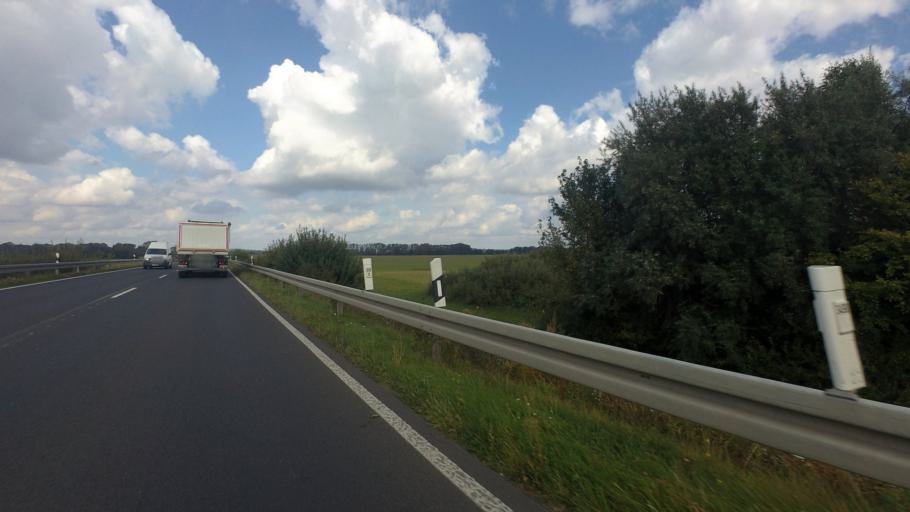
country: DE
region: Brandenburg
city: Juterbog
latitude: 51.9912
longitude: 13.1078
